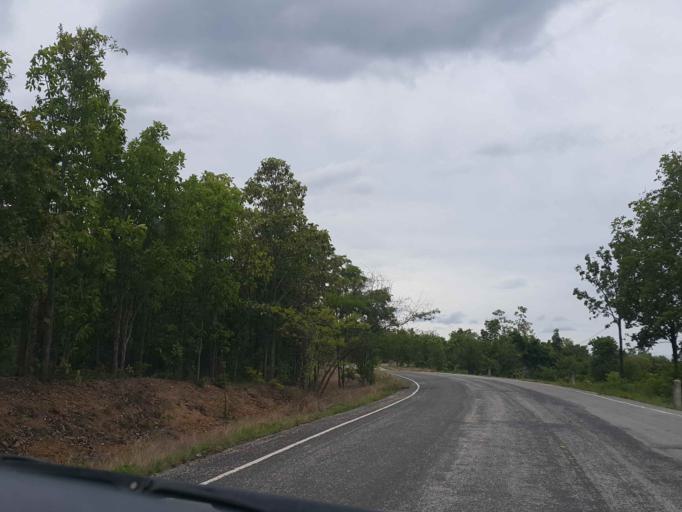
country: TH
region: Chiang Mai
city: Doi Lo
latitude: 18.4985
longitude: 98.7597
